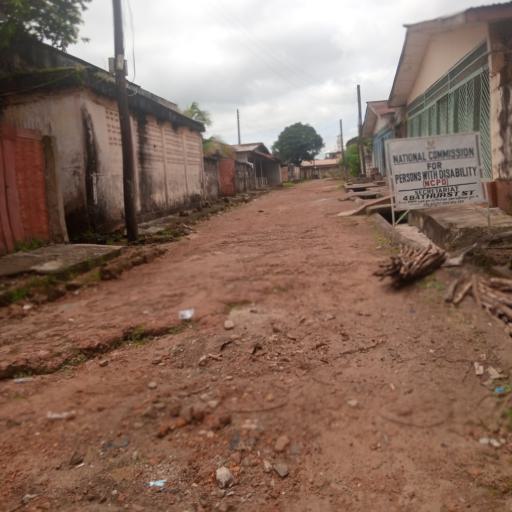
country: SL
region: Eastern Province
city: Kenema
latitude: 7.8863
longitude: -11.1874
